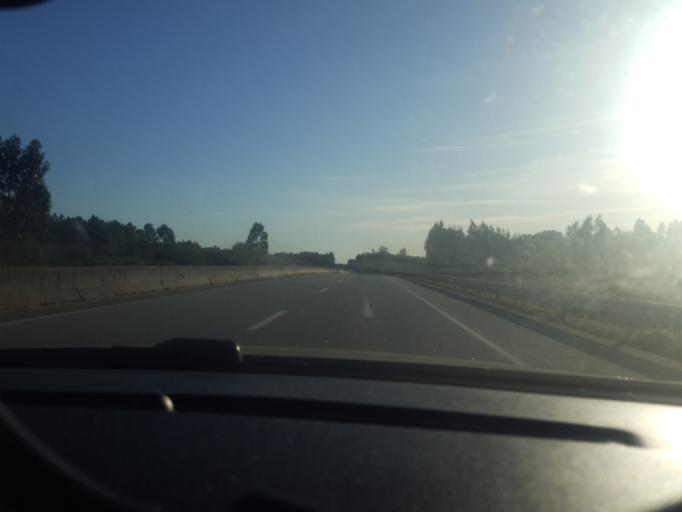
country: PT
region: Viseu
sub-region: Concelho de Carregal do Sal
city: Carregal do Sal
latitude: 40.4728
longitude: -7.9302
